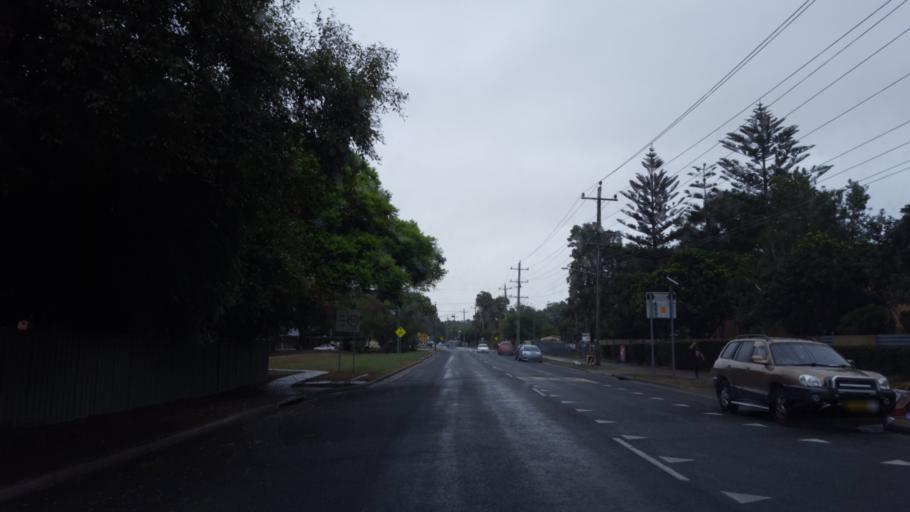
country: AU
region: New South Wales
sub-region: Port Stephens Shire
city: Anna Bay
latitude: -32.7772
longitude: 152.0878
